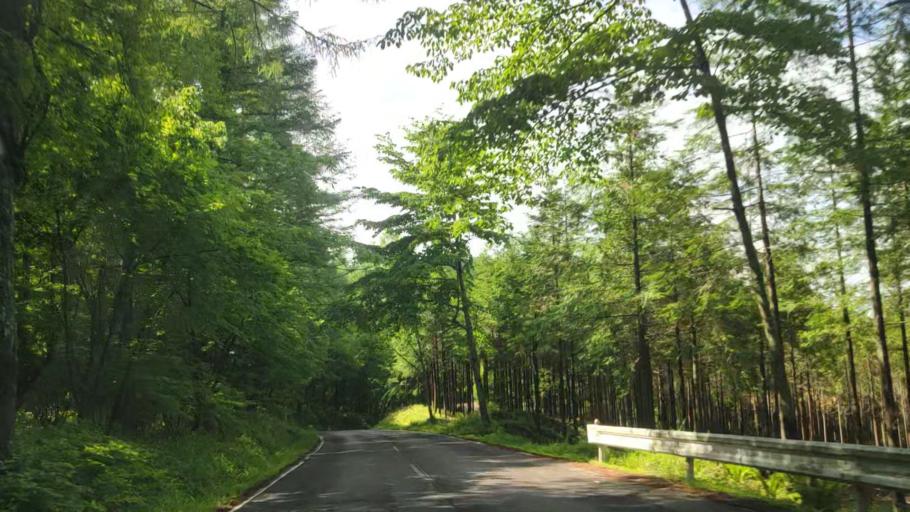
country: JP
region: Nagano
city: Suwa
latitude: 36.0884
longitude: 138.1475
